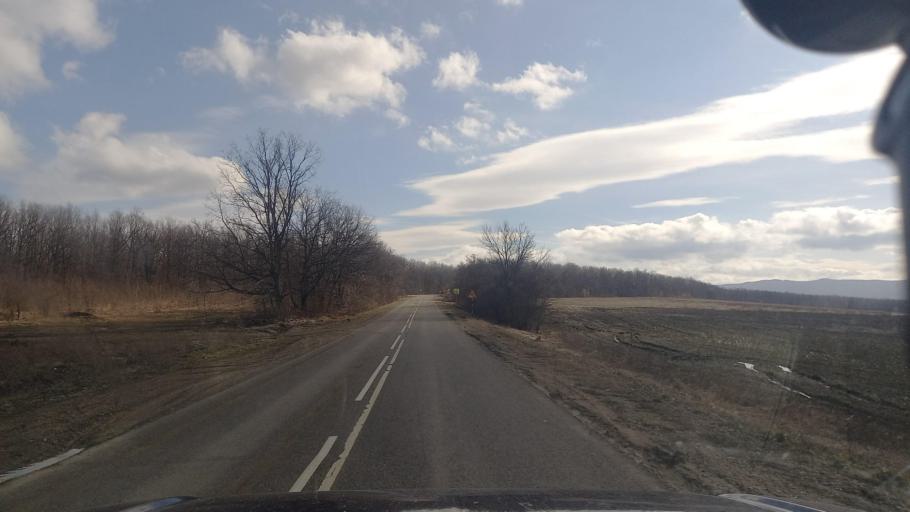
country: RU
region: Krasnodarskiy
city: Novodmitriyevskaya
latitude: 44.7451
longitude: 38.9960
